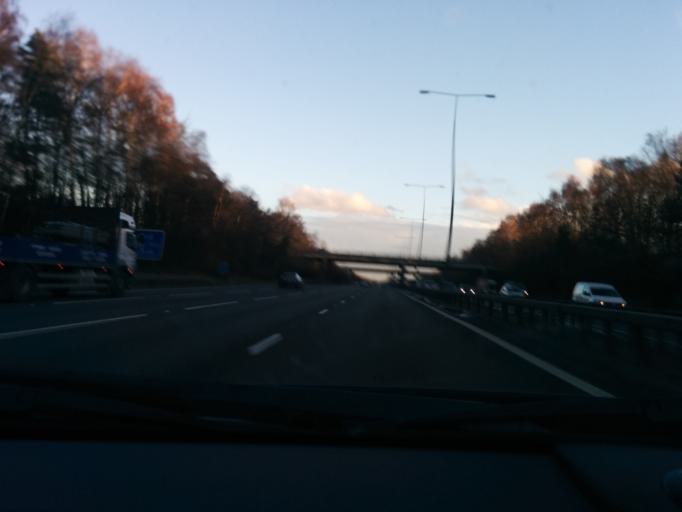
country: GB
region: England
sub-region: Buckinghamshire
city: Beaconsfield
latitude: 51.5953
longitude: -0.6306
